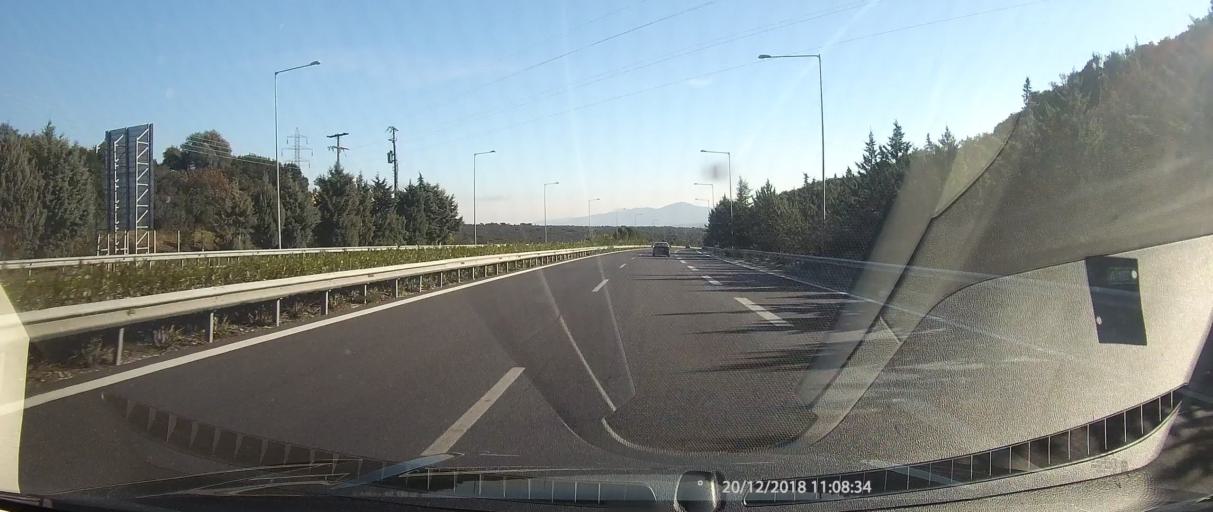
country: GR
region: Peloponnese
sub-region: Nomos Korinthias
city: Ayios Vasilios
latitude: 37.8037
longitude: 22.7359
